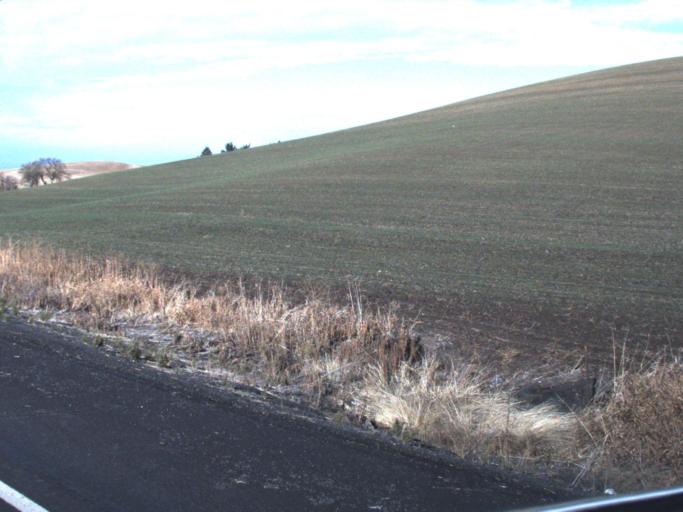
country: US
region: Washington
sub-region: Whitman County
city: Pullman
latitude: 46.7354
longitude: -117.2214
